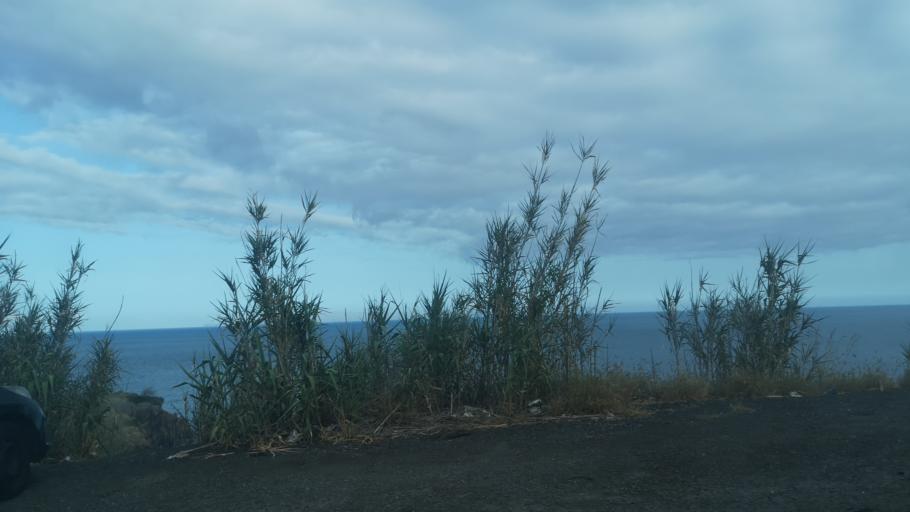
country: PT
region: Madeira
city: Canico
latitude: 32.6512
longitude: -16.8228
